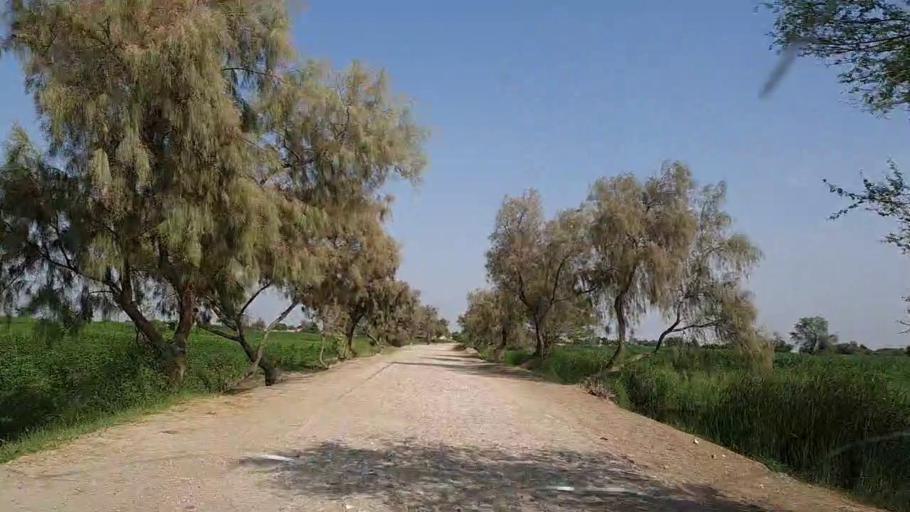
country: PK
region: Sindh
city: Khanpur
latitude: 27.7330
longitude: 69.3561
